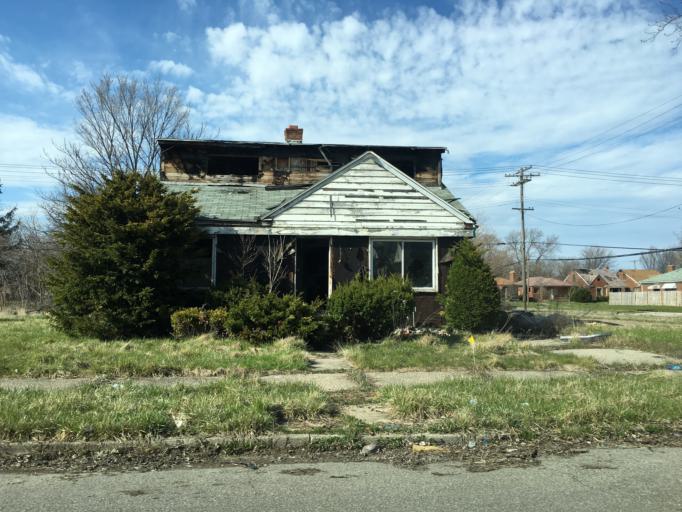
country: US
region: Michigan
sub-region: Wayne County
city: Harper Woods
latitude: 42.4247
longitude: -82.9680
